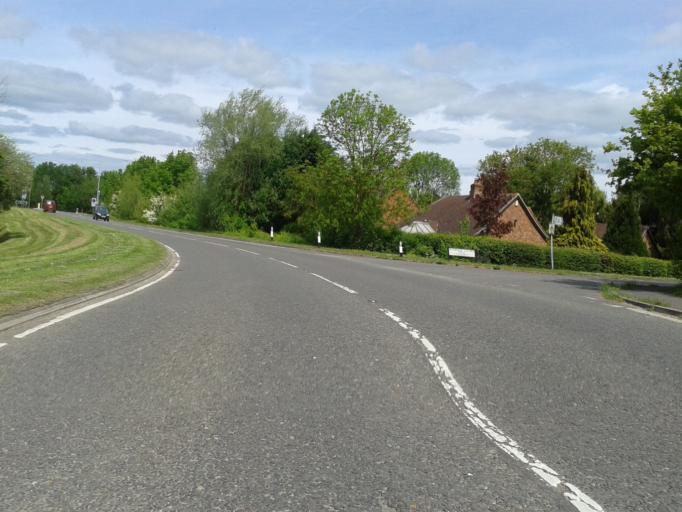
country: GB
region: England
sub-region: Cambridgeshire
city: Melbourn
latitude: 52.0994
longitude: 0.0366
